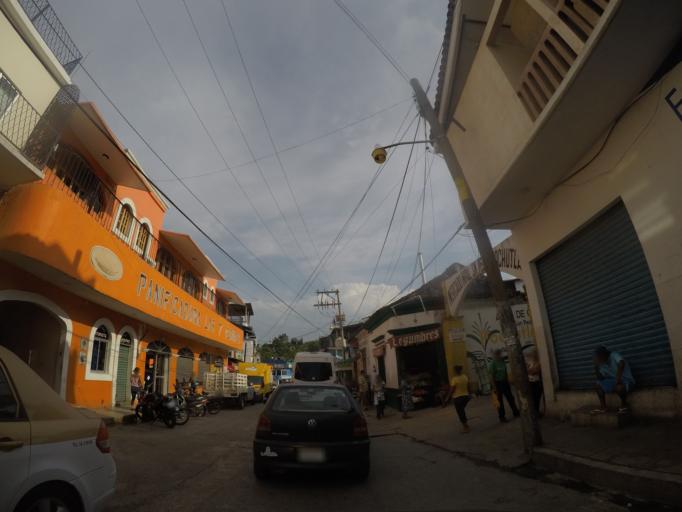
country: MX
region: Oaxaca
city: San Pedro Pochutla
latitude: 15.7472
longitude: -96.4667
